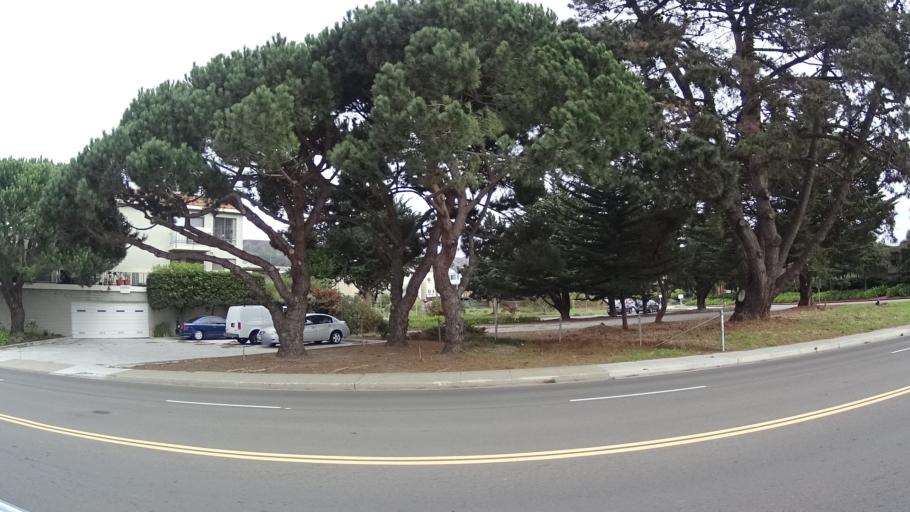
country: US
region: California
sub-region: San Mateo County
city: Colma
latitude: 37.6594
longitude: -122.4366
